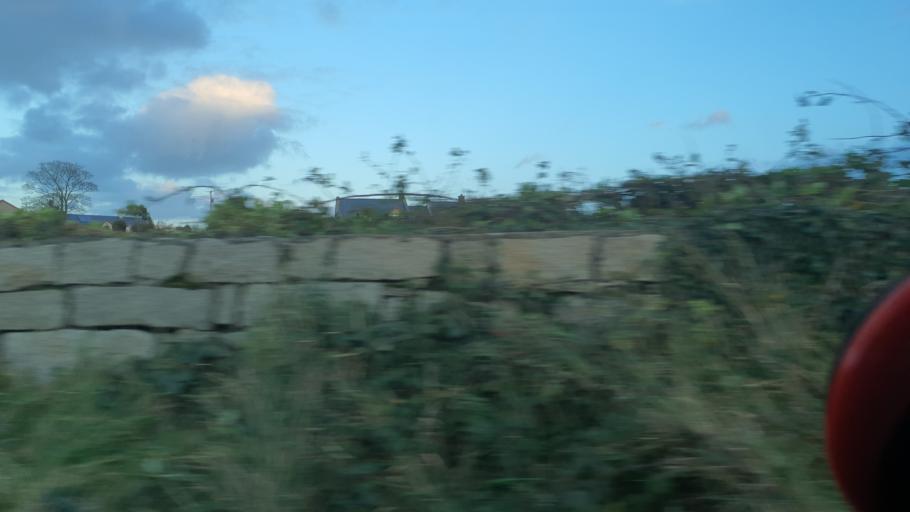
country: GB
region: Northern Ireland
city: Kilkeel
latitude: 54.0452
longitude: -6.0684
